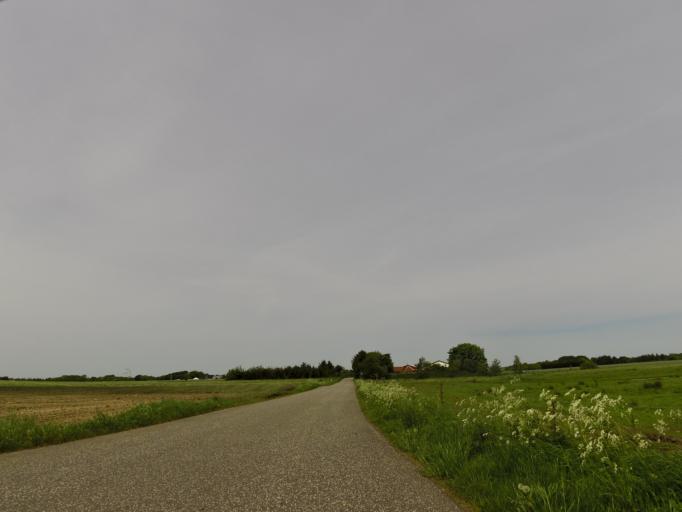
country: DK
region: Central Jutland
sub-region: Holstebro Kommune
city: Vinderup
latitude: 56.5597
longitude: 8.8903
